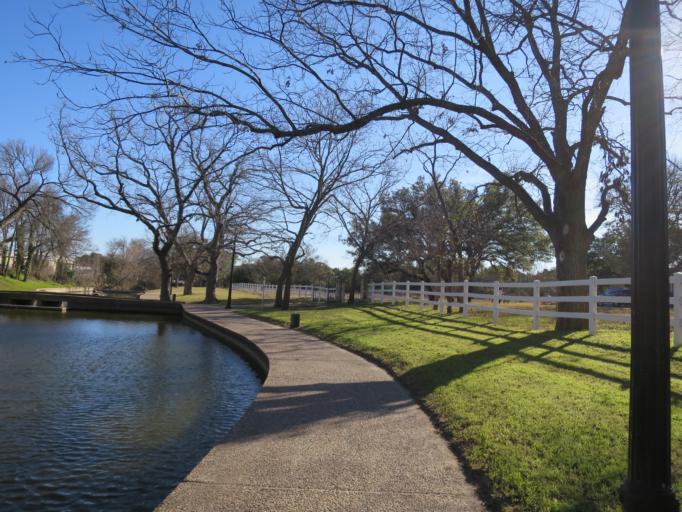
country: US
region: Texas
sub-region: Burnet County
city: Burnet
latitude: 30.7536
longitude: -98.2289
